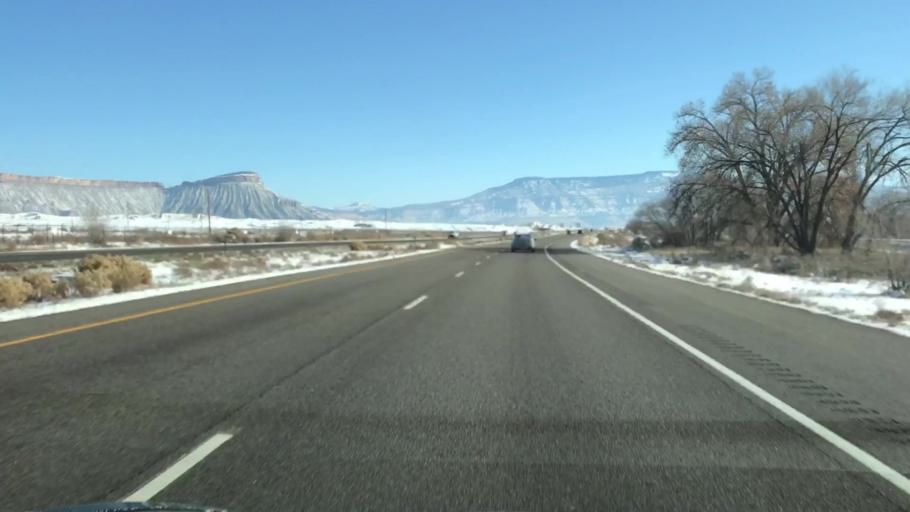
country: US
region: Colorado
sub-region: Mesa County
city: Fruitvale
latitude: 39.1086
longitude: -108.5043
